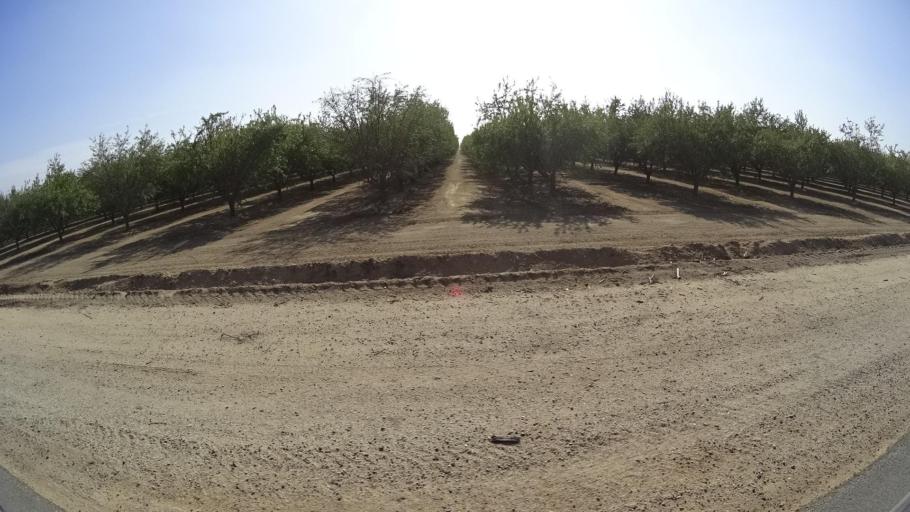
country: US
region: California
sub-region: Kern County
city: Shafter
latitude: 35.5296
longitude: -119.1794
